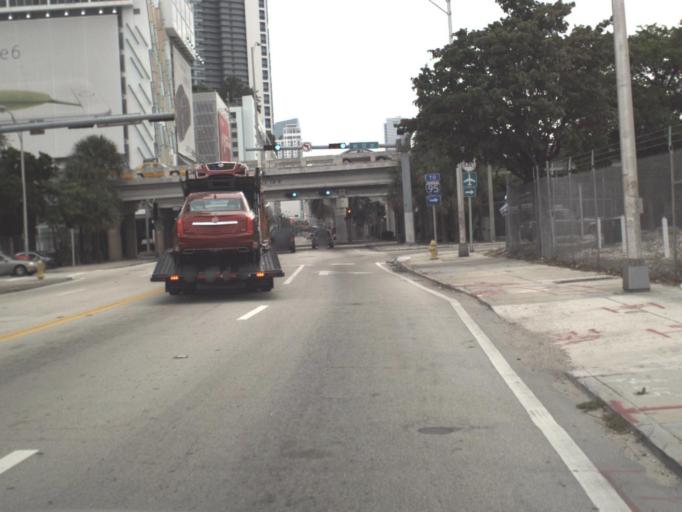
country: US
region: Florida
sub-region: Miami-Dade County
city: Miami
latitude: 25.7865
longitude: -80.1907
